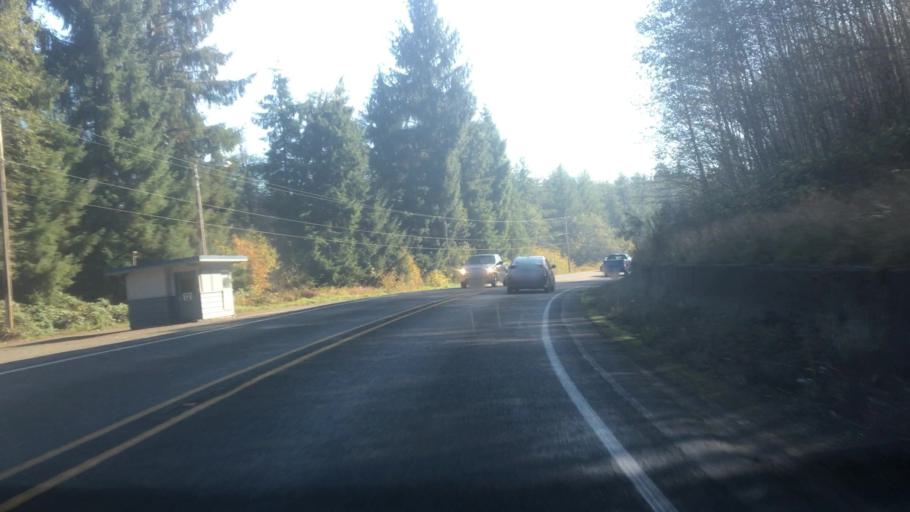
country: US
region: Washington
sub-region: Grays Harbor County
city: Central Park
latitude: 46.9149
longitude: -123.7170
